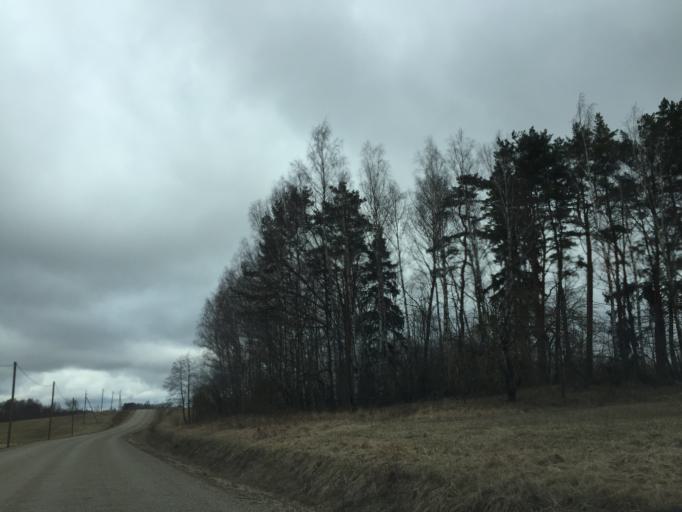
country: LV
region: Ilukste
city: Ilukste
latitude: 56.0356
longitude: 26.2052
